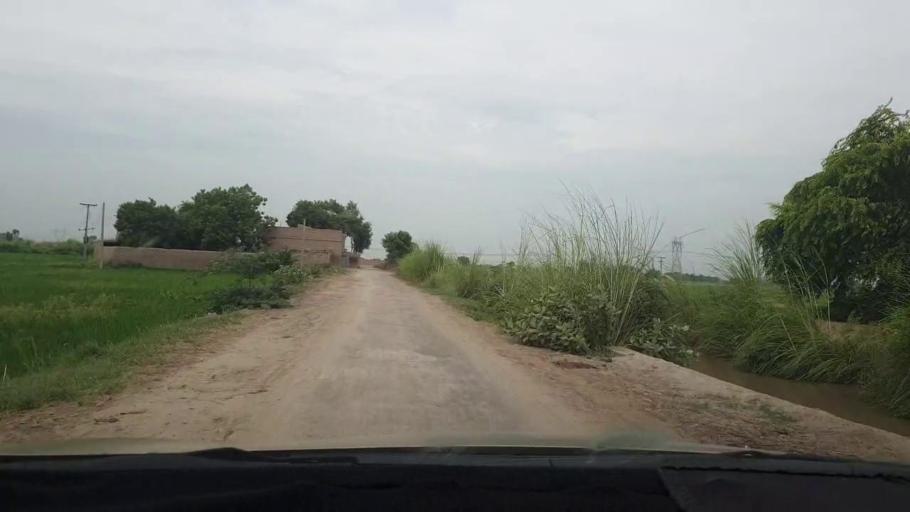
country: PK
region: Sindh
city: Naudero
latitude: 27.6795
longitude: 68.3449
